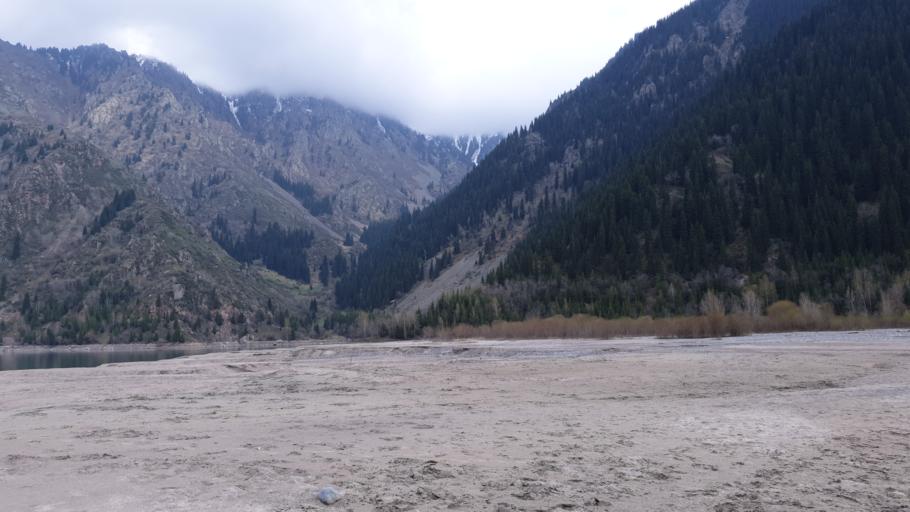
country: KZ
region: Almaty Oblysy
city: Esik
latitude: 43.2537
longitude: 77.4811
